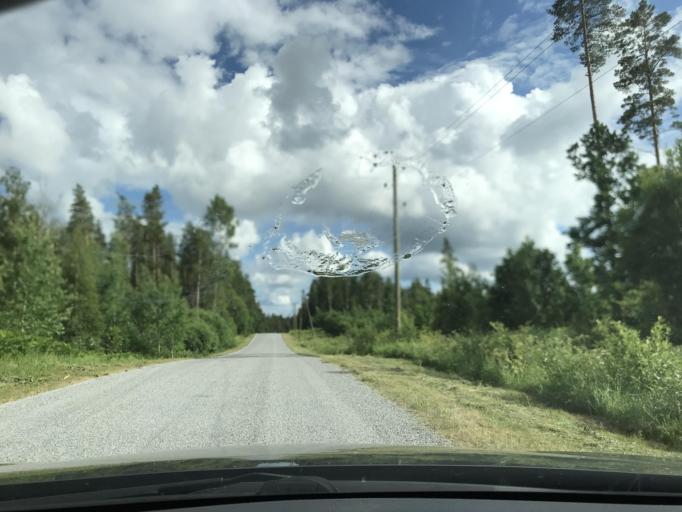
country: LV
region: Alsunga
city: Alsunga
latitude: 56.9899
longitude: 21.6274
